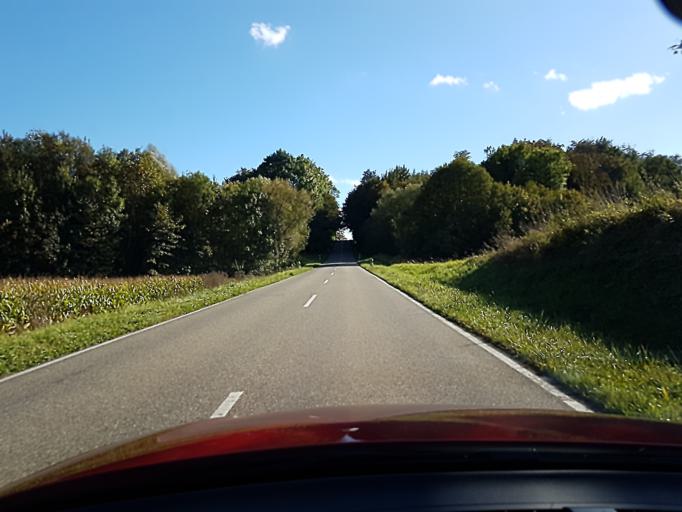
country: DE
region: Hesse
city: Neckarsteinach
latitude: 49.3740
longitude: 8.8385
